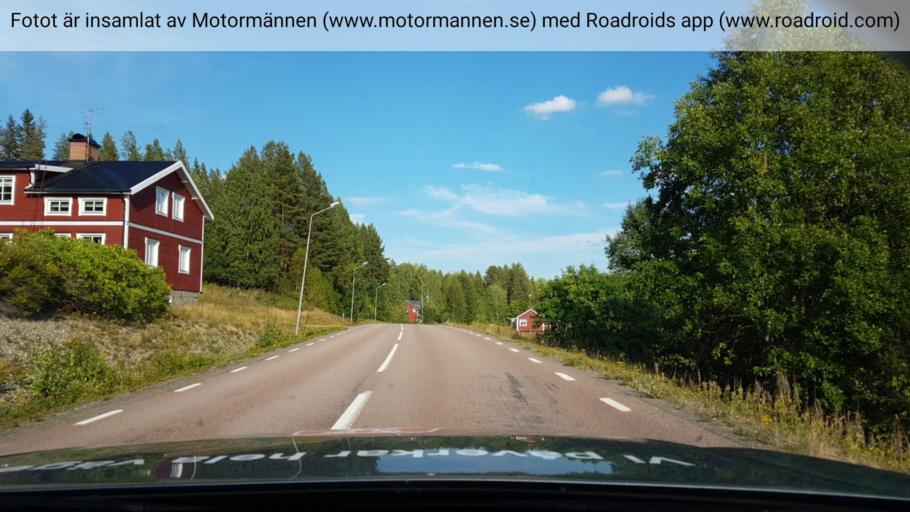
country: SE
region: Vaesternorrland
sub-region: Solleftea Kommun
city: As
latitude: 63.5936
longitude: 16.1808
